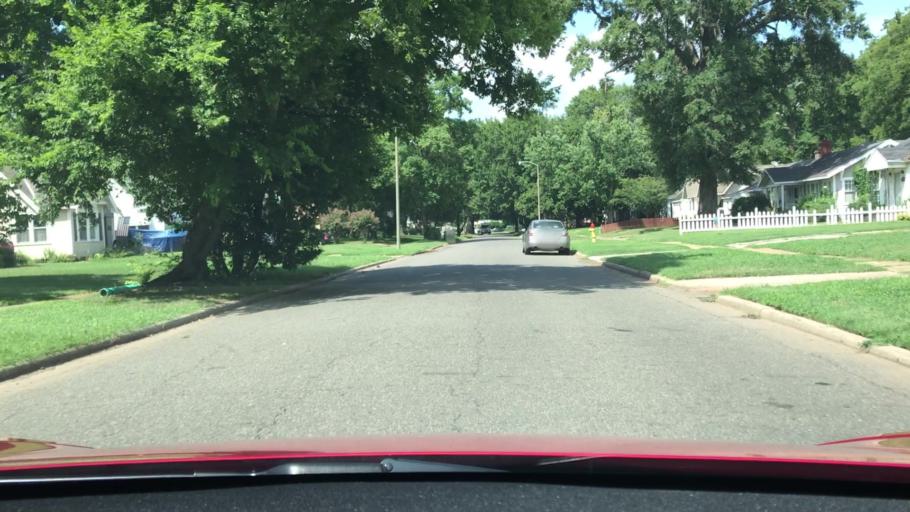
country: US
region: Louisiana
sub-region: Bossier Parish
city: Bossier City
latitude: 32.4786
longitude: -93.7270
